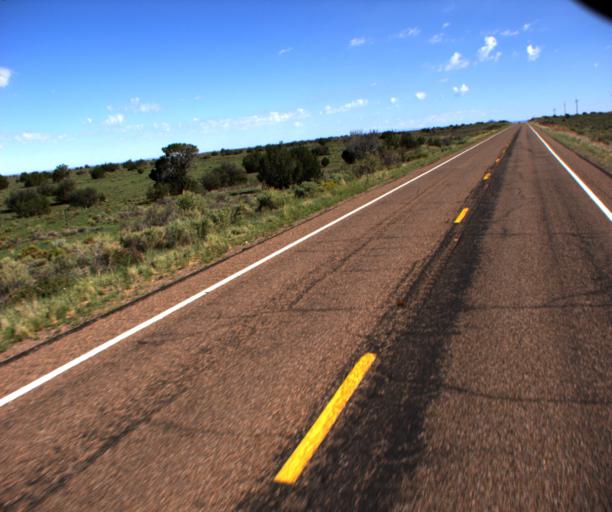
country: US
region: Arizona
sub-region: Coconino County
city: Williams
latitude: 35.5329
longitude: -112.1654
